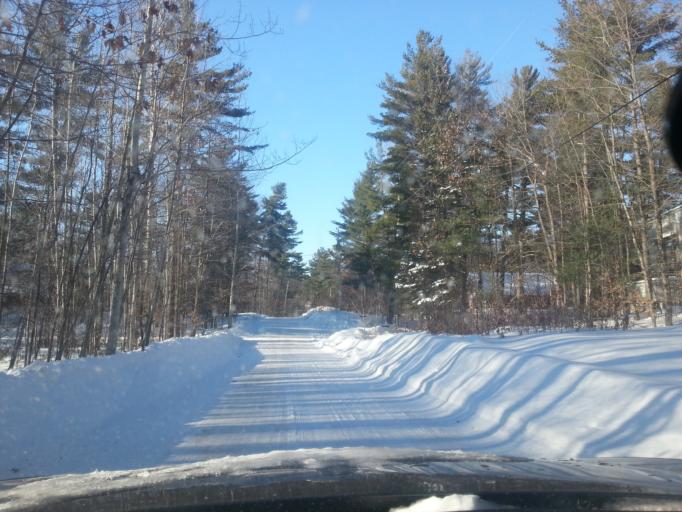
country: CA
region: Ontario
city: Arnprior
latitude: 45.3242
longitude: -76.3254
